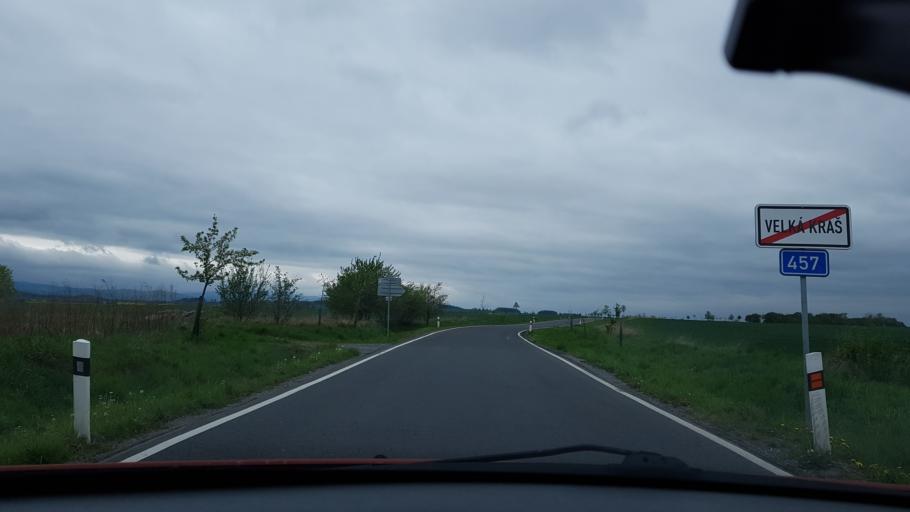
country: CZ
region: Olomoucky
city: Vidnava
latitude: 50.3744
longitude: 17.1779
